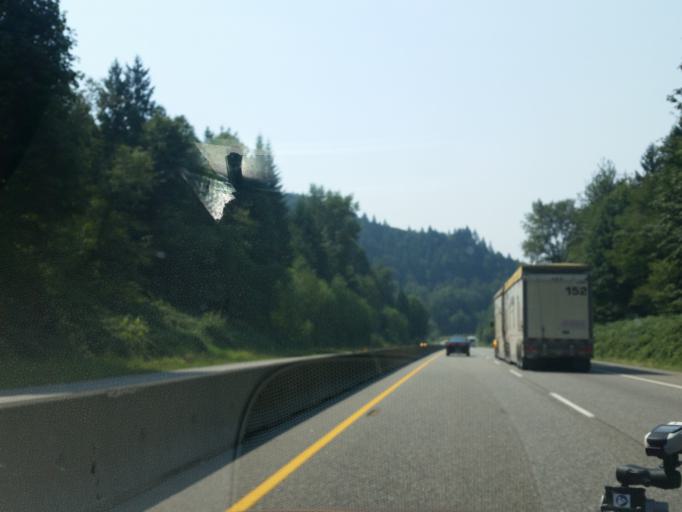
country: CA
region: British Columbia
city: Agassiz
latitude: 49.1646
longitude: -121.7918
